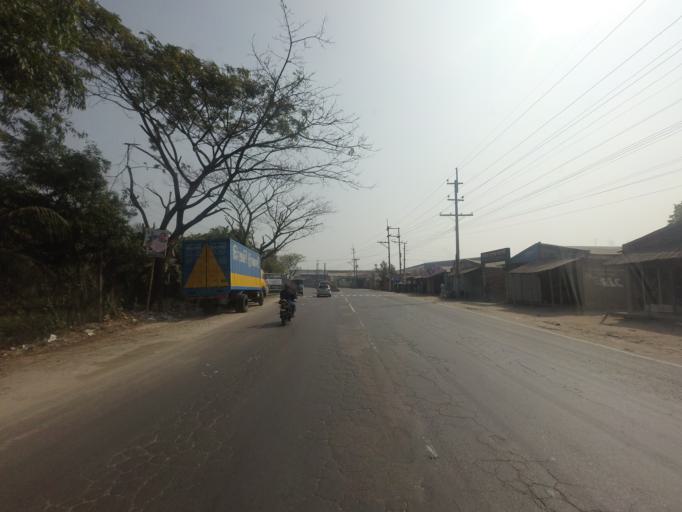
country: BD
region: Dhaka
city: Narsingdi
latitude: 23.8962
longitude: 90.6787
